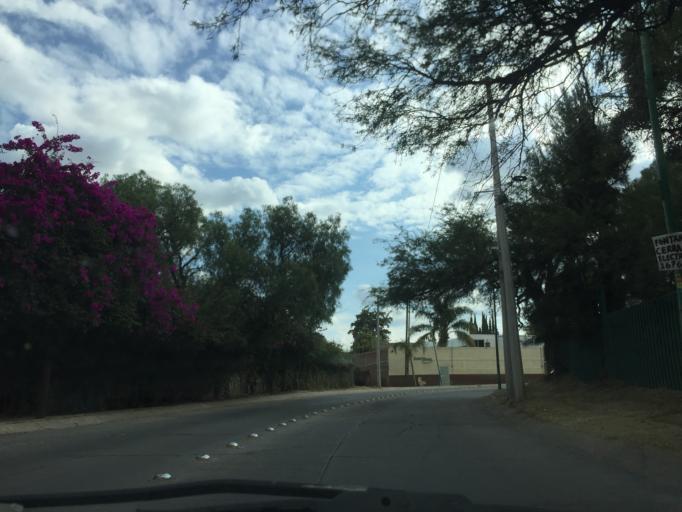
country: MX
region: Guanajuato
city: Leon
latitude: 21.1657
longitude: -101.6828
